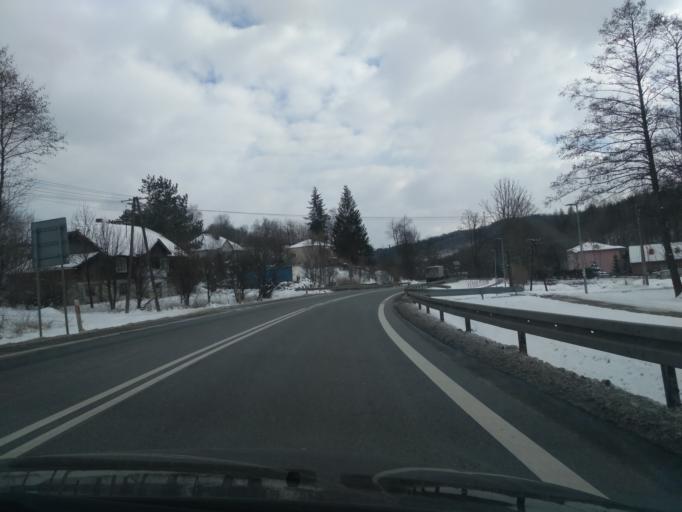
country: PL
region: Subcarpathian Voivodeship
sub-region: Powiat strzyzowski
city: Babica
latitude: 49.9258
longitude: 21.8767
